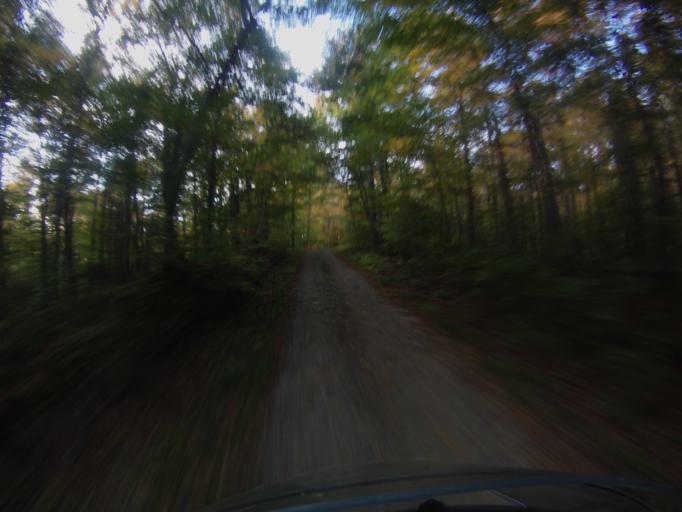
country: US
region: Vermont
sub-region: Addison County
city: Bristol
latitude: 44.0978
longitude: -72.9532
